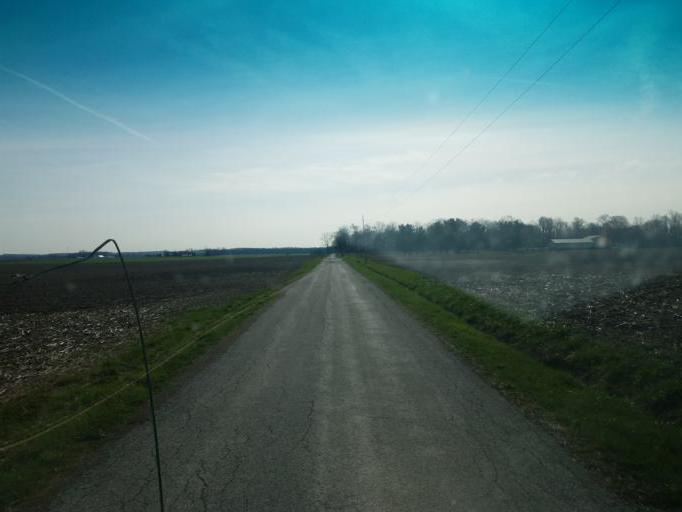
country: US
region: Ohio
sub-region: Richland County
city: Shelby
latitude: 40.8870
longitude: -82.5666
